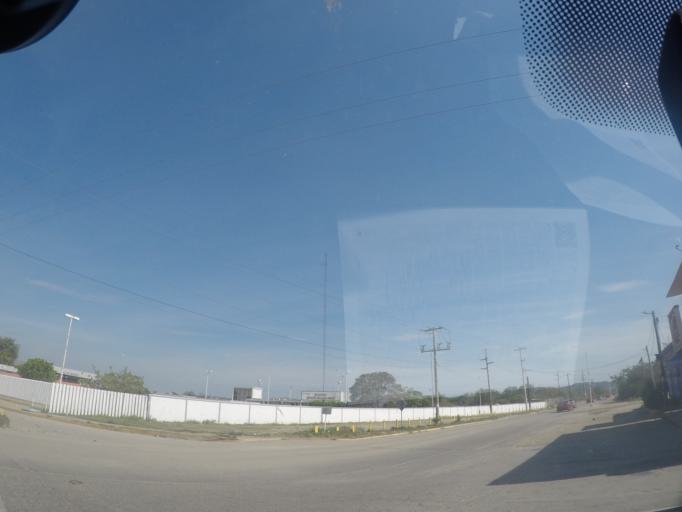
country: MX
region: Oaxaca
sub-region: Salina Cruz
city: Salina Cruz
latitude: 16.2194
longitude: -95.1904
